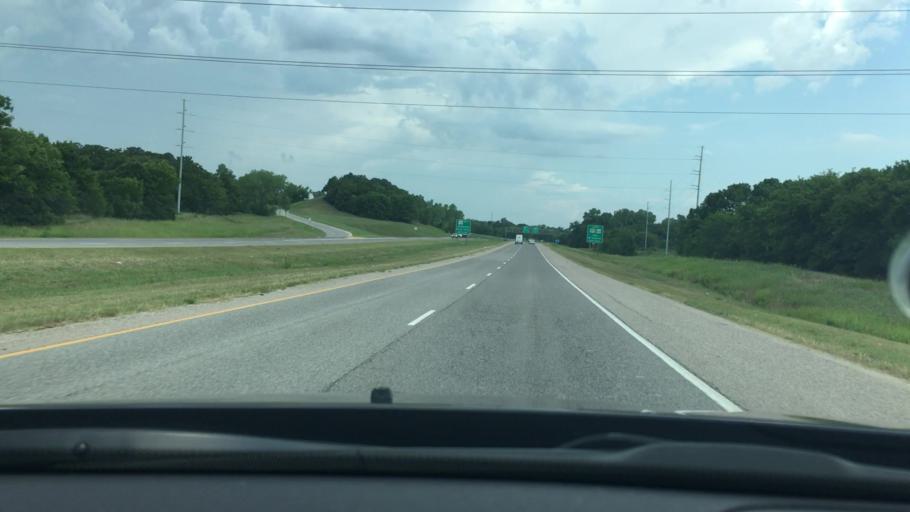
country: US
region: Oklahoma
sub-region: Pontotoc County
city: Ada
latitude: 34.7441
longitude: -96.6498
